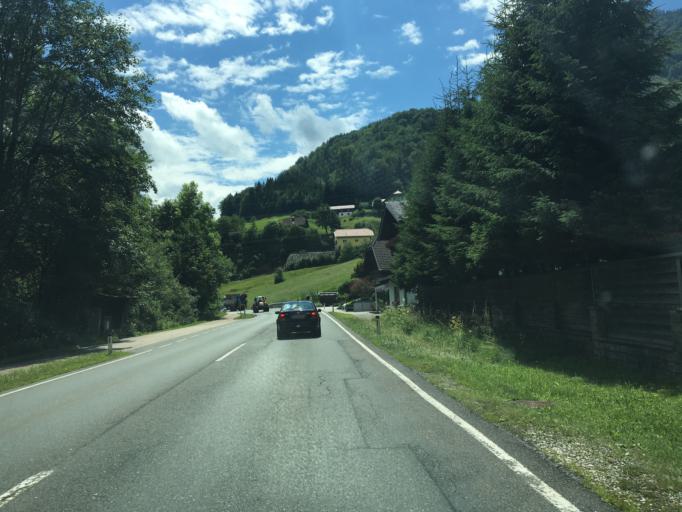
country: AT
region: Salzburg
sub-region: Politischer Bezirk Salzburg-Umgebung
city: Ebenau
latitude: 47.7670
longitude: 13.1790
